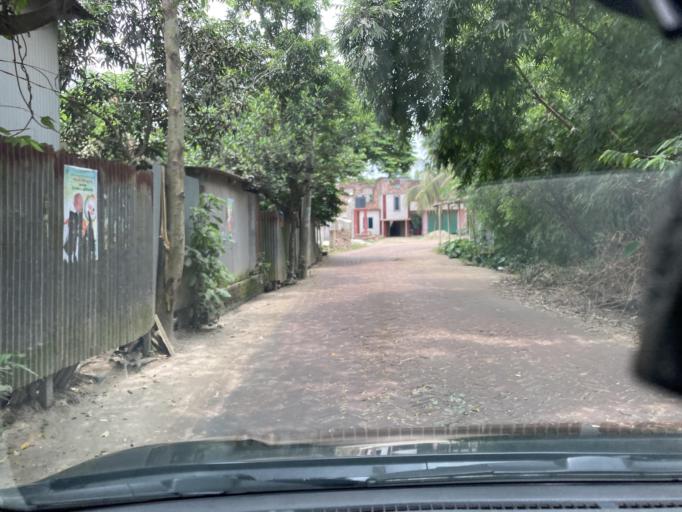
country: BD
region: Dhaka
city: Dohar
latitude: 23.8088
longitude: 90.0455
